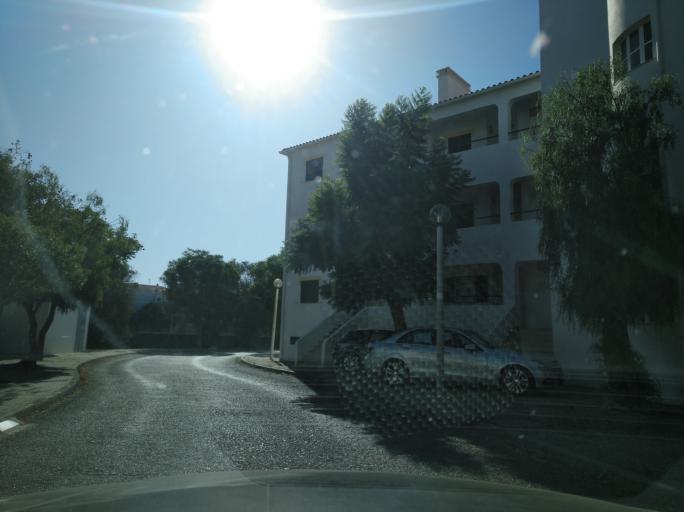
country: PT
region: Faro
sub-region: Vila Real de Santo Antonio
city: Monte Gordo
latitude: 37.1740
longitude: -7.5066
